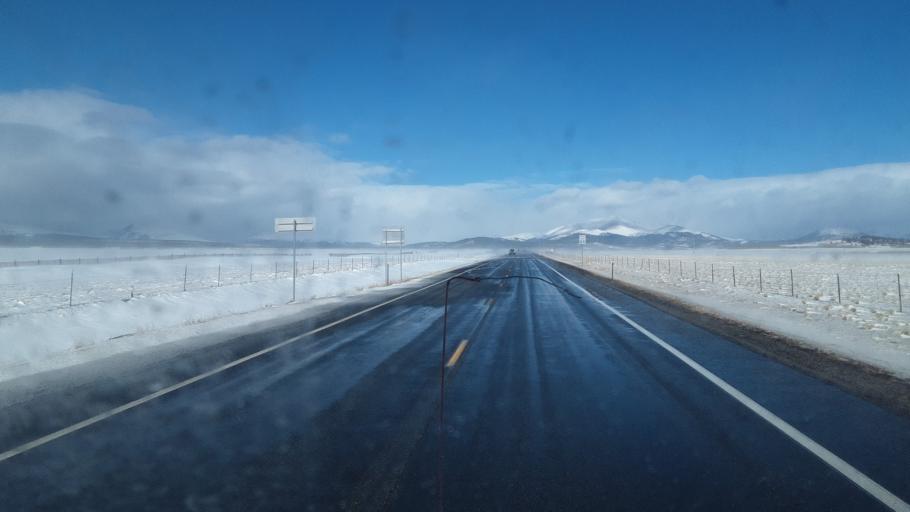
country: US
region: Colorado
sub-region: Park County
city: Fairplay
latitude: 39.1545
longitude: -105.9992
